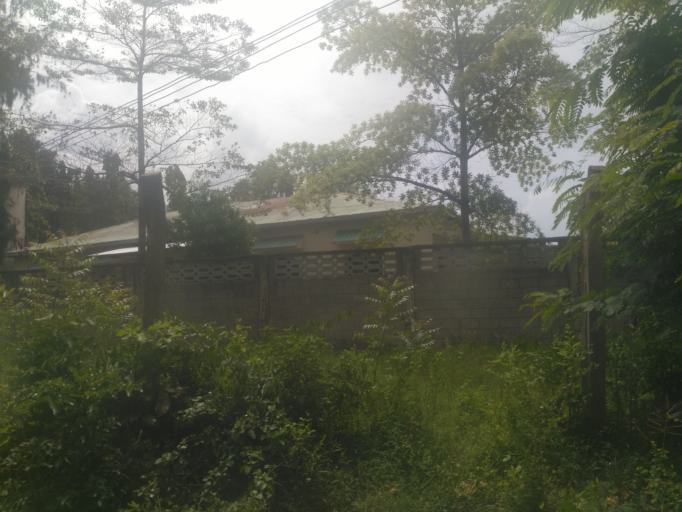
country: TZ
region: Zanzibar Urban/West
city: Zanzibar
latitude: -6.2296
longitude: 39.2125
